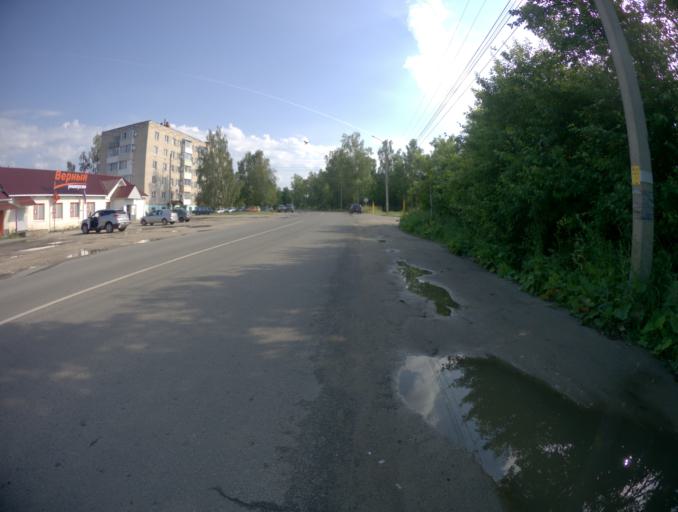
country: RU
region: Vladimir
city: Novovyazniki
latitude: 56.2296
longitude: 42.1965
